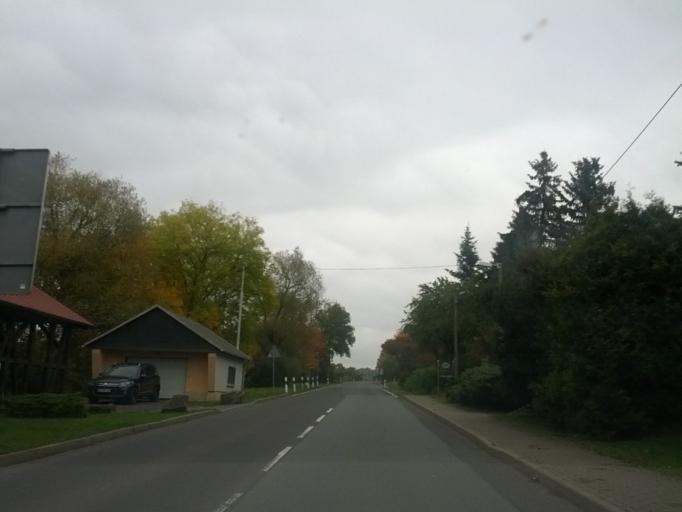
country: DE
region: Thuringia
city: Klettbach
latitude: 50.9164
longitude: 11.1530
